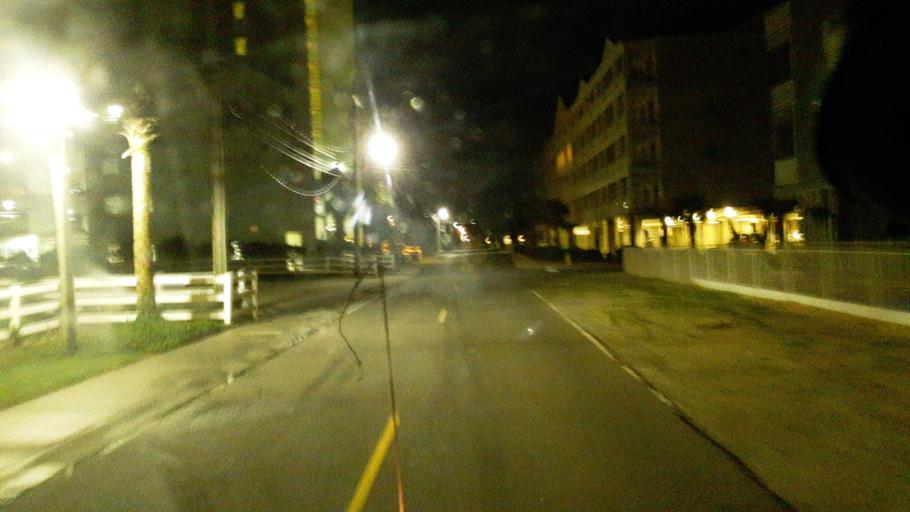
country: US
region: South Carolina
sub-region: Horry County
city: Little River
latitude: 33.8374
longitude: -78.6135
